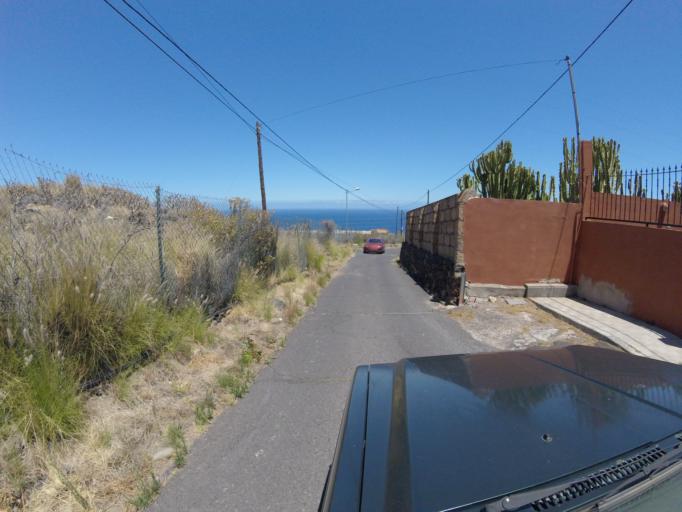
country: ES
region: Canary Islands
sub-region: Provincia de Santa Cruz de Tenerife
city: Candelaria
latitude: 28.3658
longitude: -16.3792
